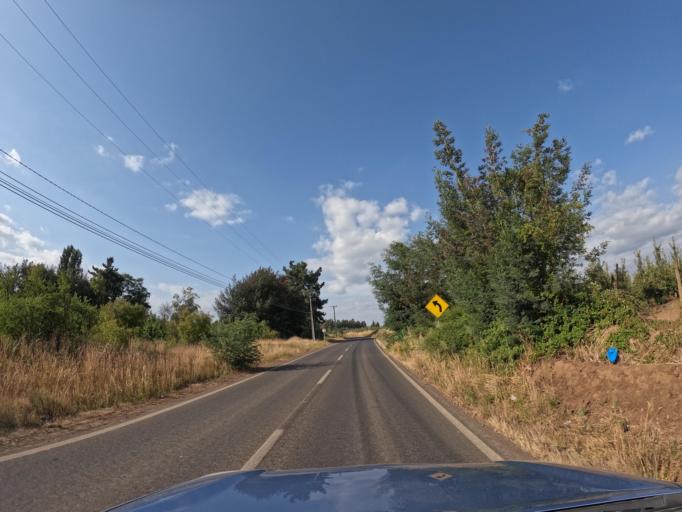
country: CL
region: Maule
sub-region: Provincia de Curico
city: Molina
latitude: -35.2643
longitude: -71.2447
